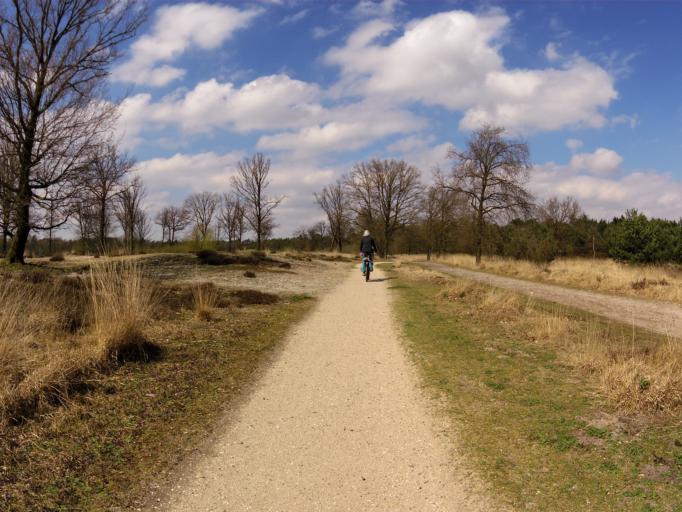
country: NL
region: North Brabant
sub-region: Gemeente Haaren
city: Haaren
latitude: 51.5727
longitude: 5.2500
